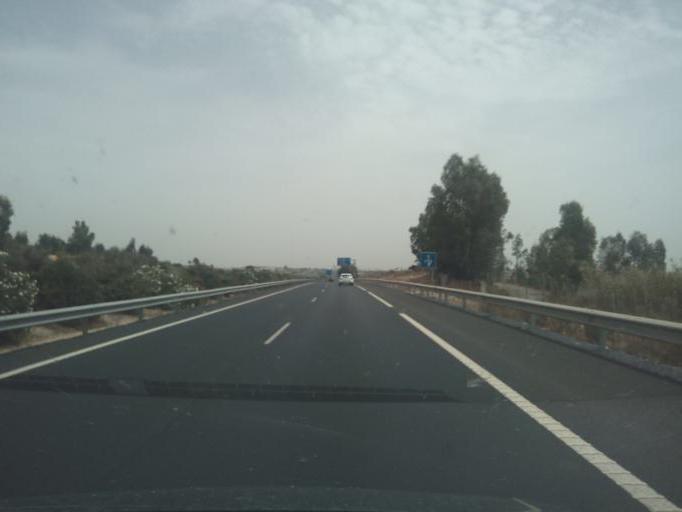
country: ES
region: Andalusia
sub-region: Provincia de Huelva
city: Bollullos par del Condado
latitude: 37.3527
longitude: -6.5722
